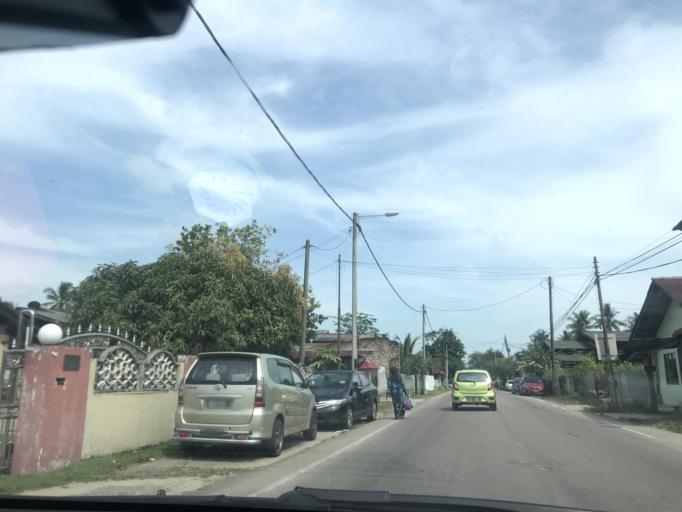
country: MY
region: Kelantan
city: Tumpat
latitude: 6.2005
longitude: 102.1610
